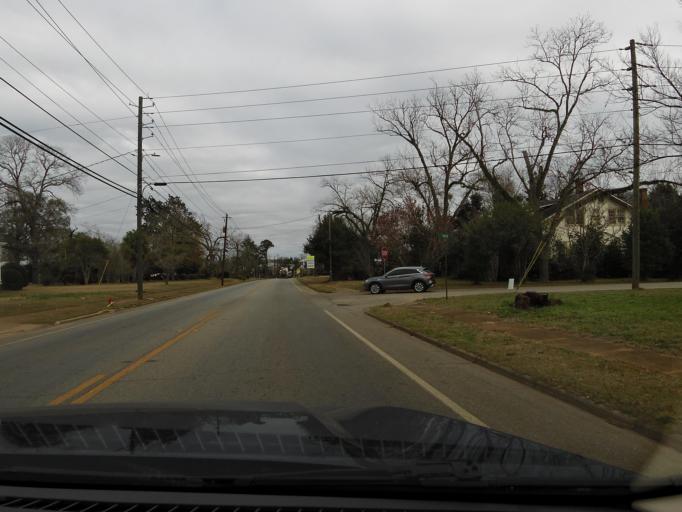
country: US
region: Georgia
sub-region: Randolph County
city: Cuthbert
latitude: 31.7706
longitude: -84.8008
